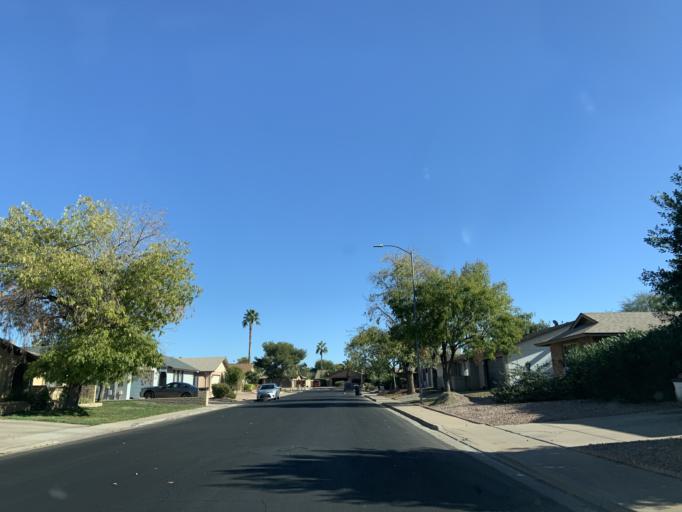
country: US
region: Arizona
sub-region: Maricopa County
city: San Carlos
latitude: 33.3717
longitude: -111.8634
